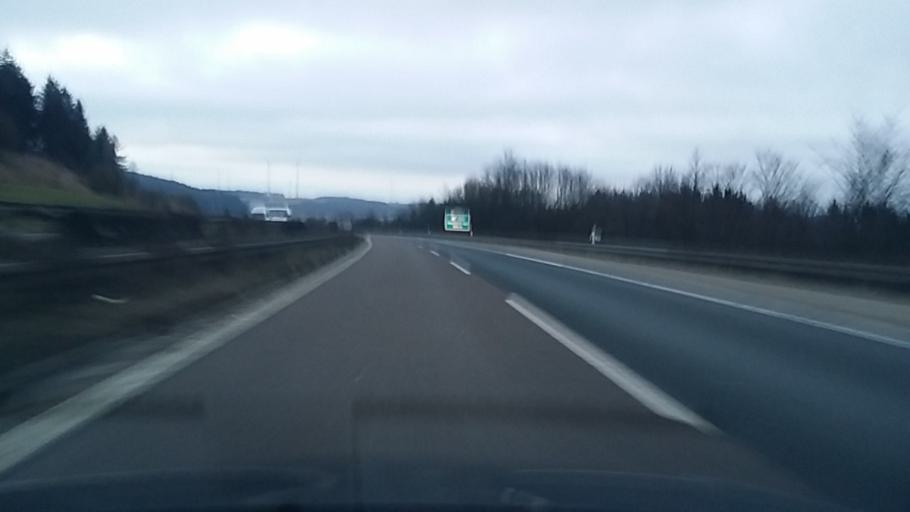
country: DE
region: Bavaria
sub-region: Upper Palatinate
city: Deining
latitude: 49.2777
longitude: 11.5962
